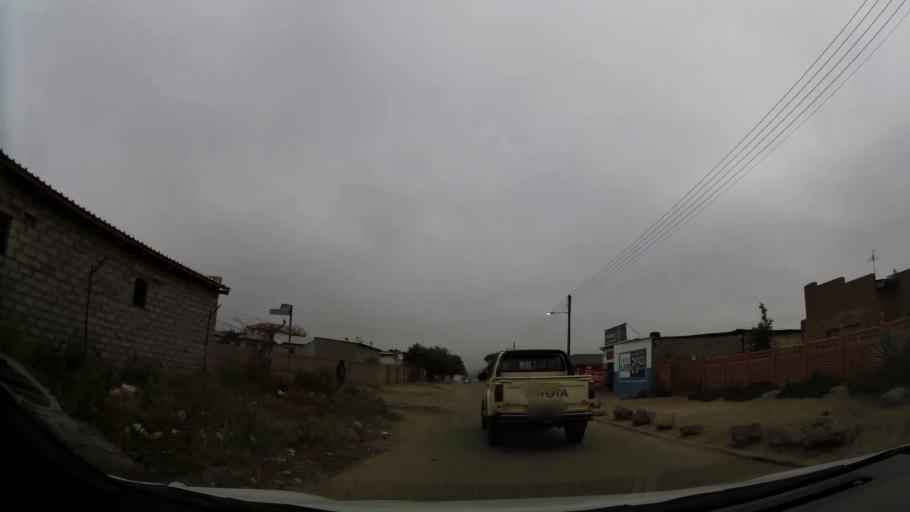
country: ZA
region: Limpopo
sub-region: Capricorn District Municipality
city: Polokwane
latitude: -23.8381
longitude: 29.3921
